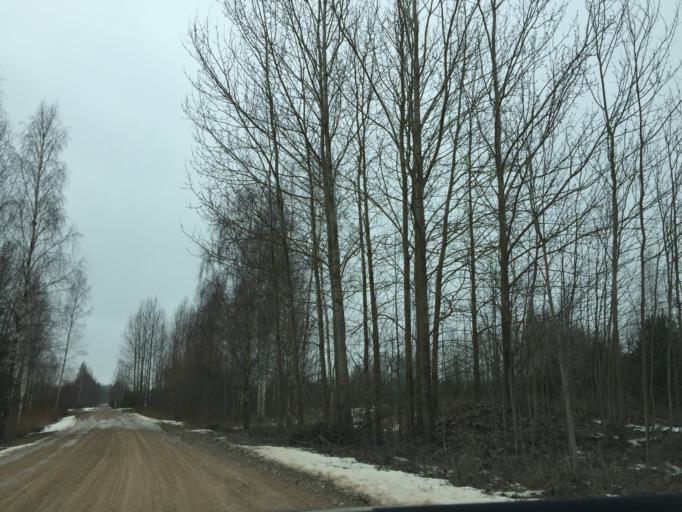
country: LV
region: Lecava
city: Iecava
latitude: 56.5702
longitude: 24.0572
